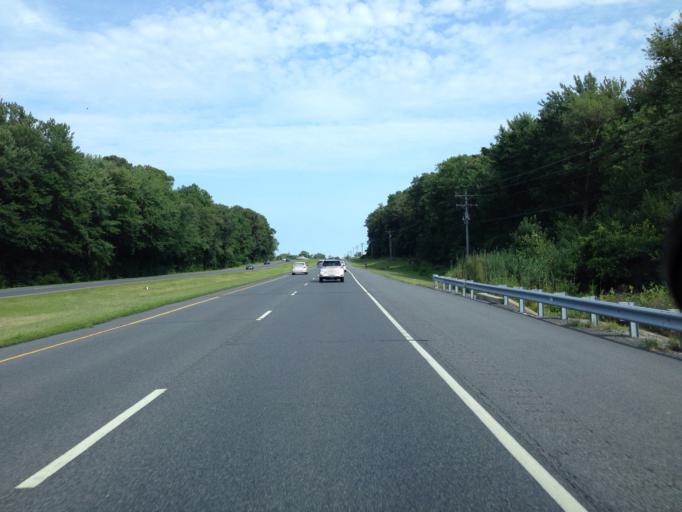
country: US
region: Delaware
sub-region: Sussex County
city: Milton
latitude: 38.8105
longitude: -75.2853
